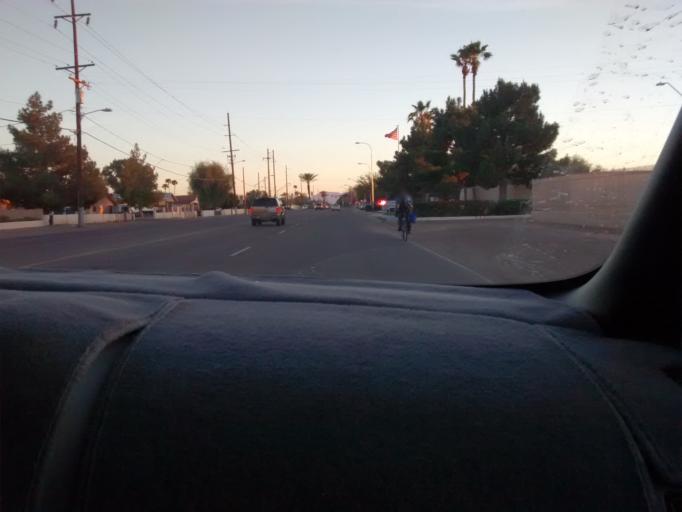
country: US
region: Arizona
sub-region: Maricopa County
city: Glendale
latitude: 33.5410
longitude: -112.2031
